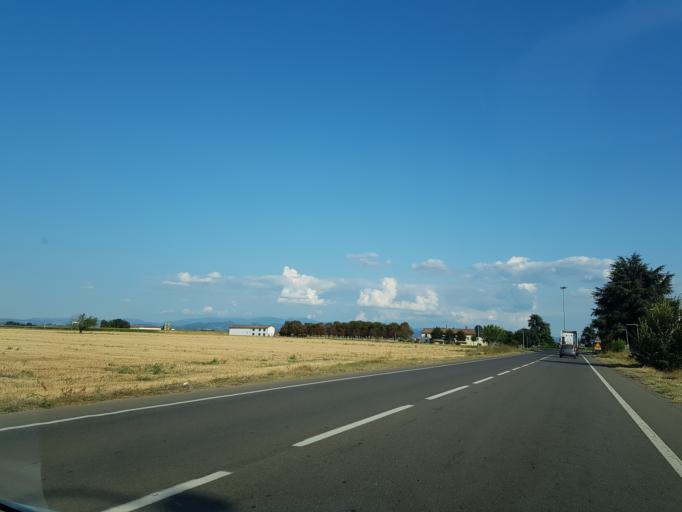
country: IT
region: Piedmont
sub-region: Provincia di Alessandria
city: Mandrogne
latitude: 44.8394
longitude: 8.7317
